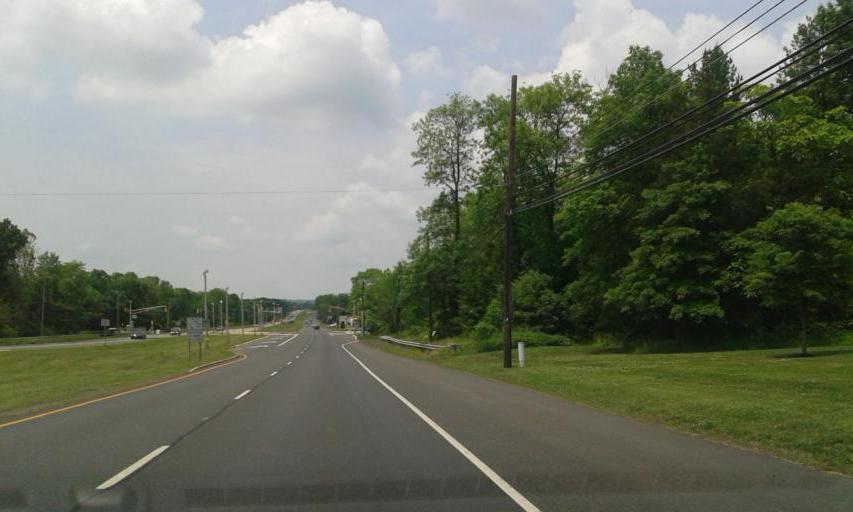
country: US
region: New Jersey
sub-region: Hunterdon County
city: Whitehouse Station
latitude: 40.6307
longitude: -74.7789
